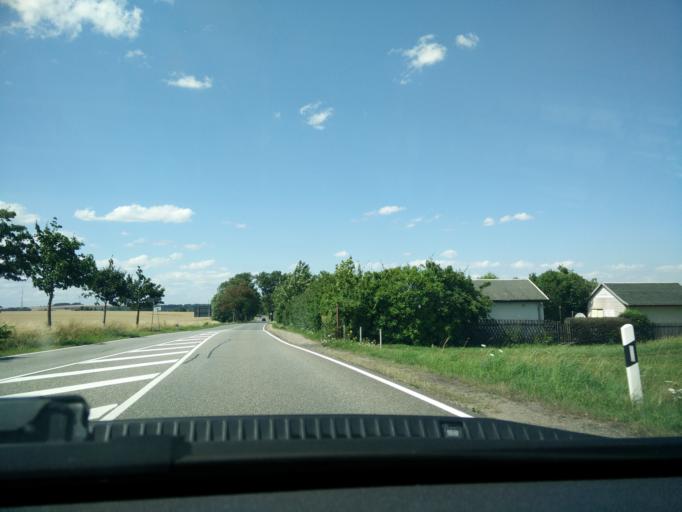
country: DE
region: Saxony
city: Penig
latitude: 50.9215
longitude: 12.7145
